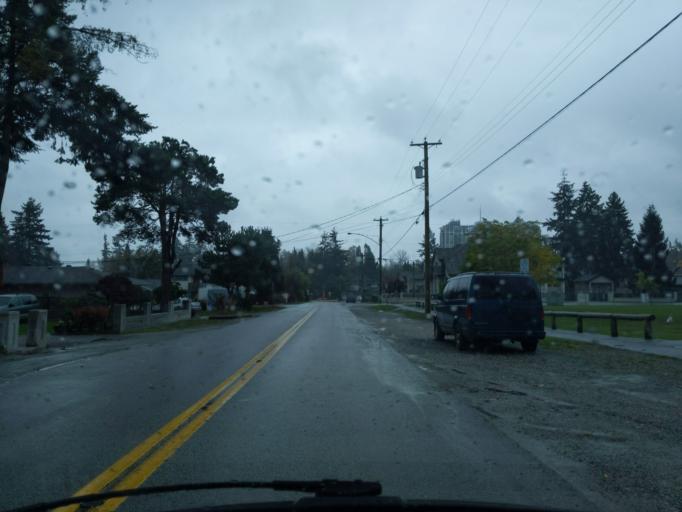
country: CA
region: British Columbia
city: New Westminster
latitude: 49.2009
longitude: -122.8589
